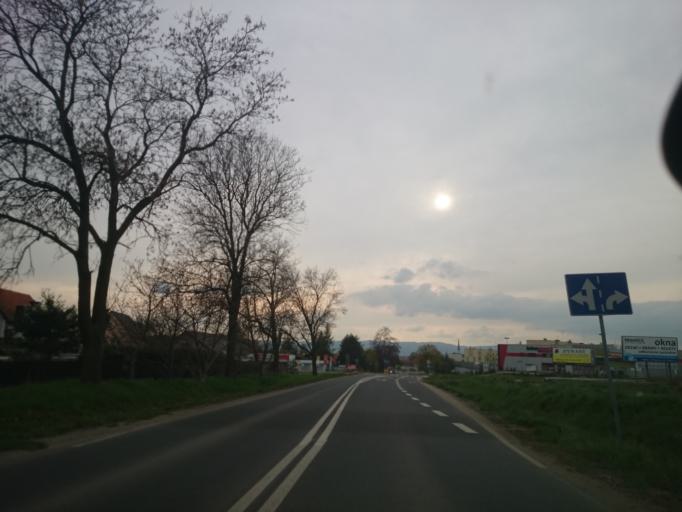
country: PL
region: Lower Silesian Voivodeship
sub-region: Powiat zabkowicki
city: Zabkowice Slaskie
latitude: 50.5876
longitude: 16.8309
